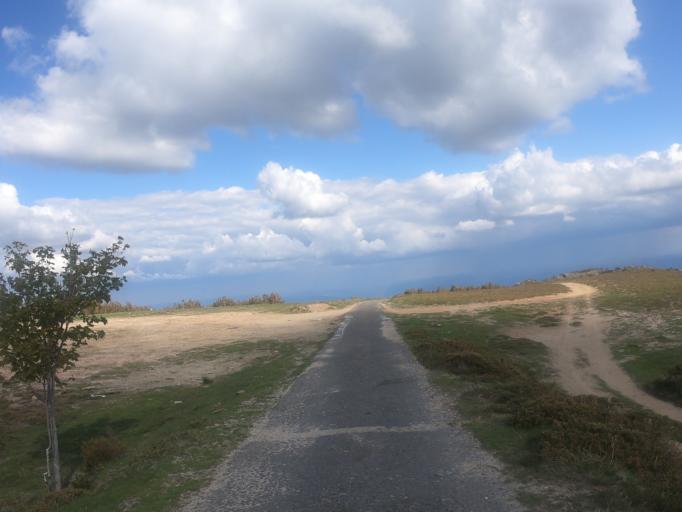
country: PT
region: Vila Real
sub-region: Mesao Frio
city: Mesao Frio
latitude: 41.2479
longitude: -7.8835
